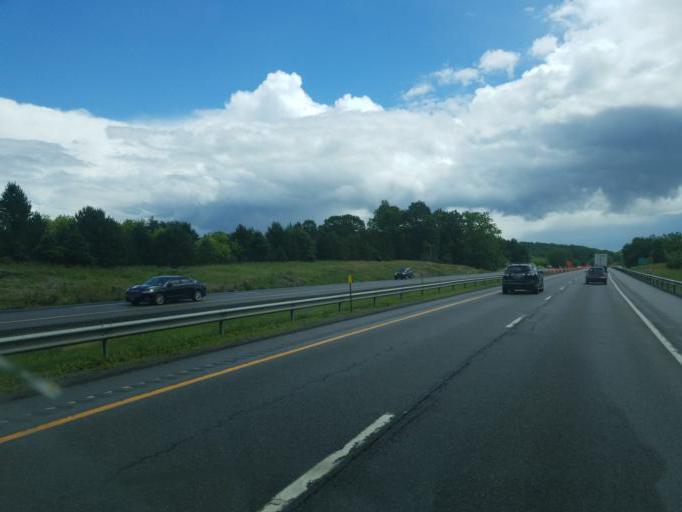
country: US
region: New York
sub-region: Ontario County
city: Victor
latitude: 43.0133
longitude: -77.4566
